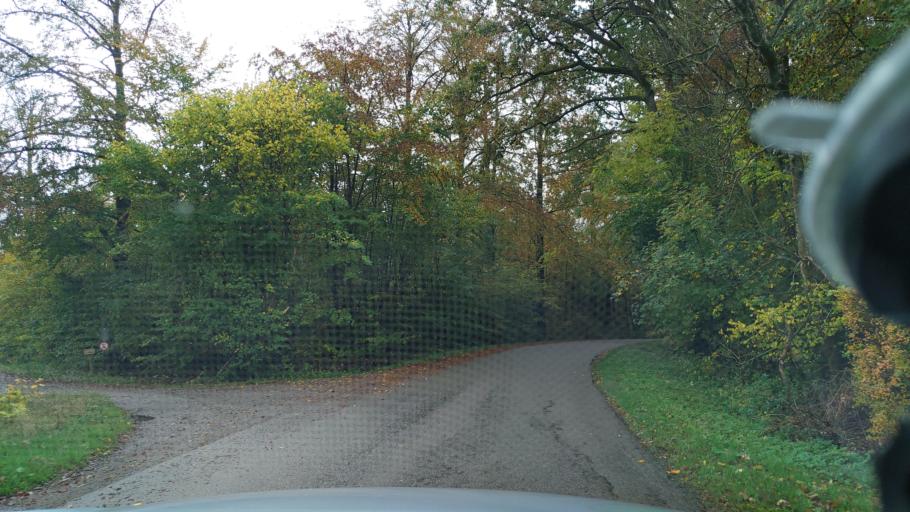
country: DK
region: Zealand
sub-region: Faxe Kommune
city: Ronnede
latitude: 55.2554
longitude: 11.9609
